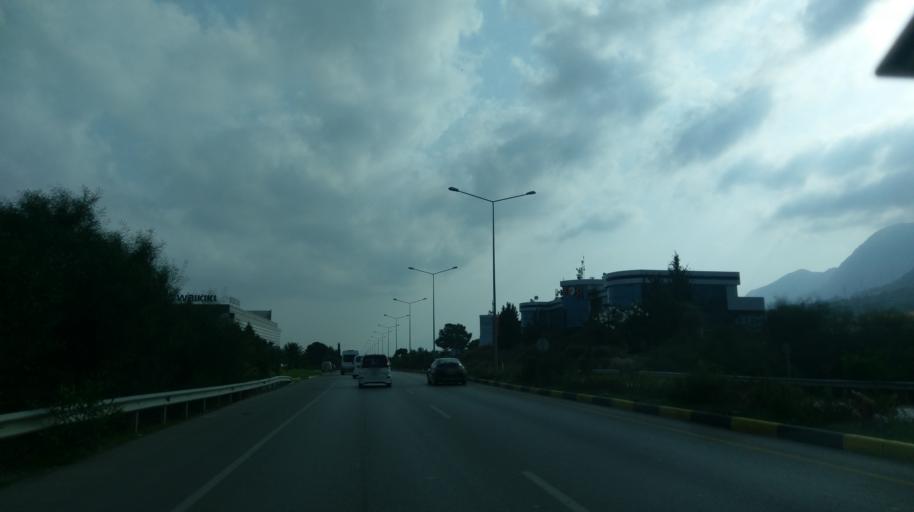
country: CY
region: Keryneia
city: Kyrenia
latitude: 35.3281
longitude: 33.2999
